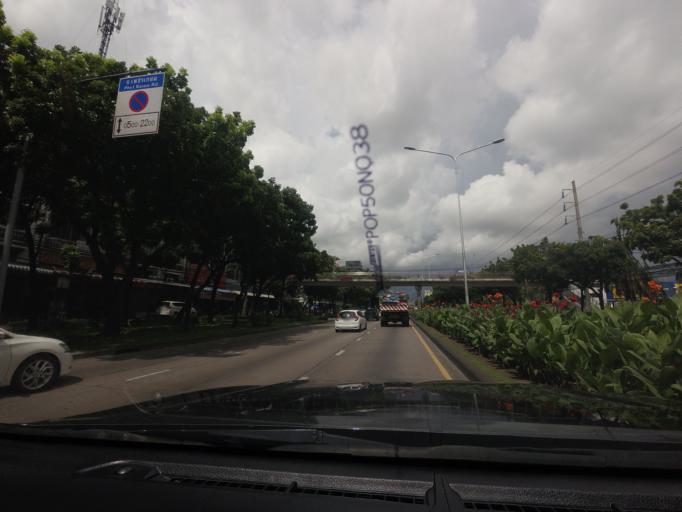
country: TH
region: Bangkok
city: Nong Khaem
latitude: 13.7072
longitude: 100.3675
